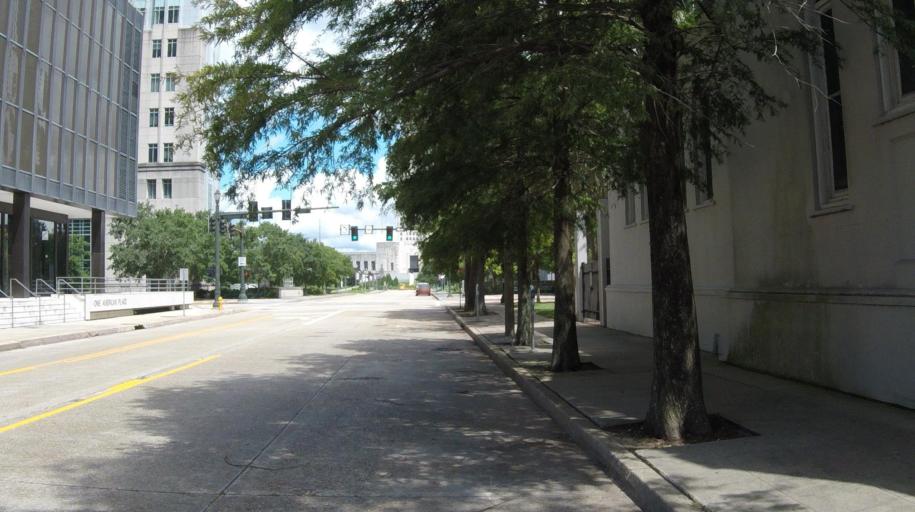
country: US
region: Louisiana
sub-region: West Baton Rouge Parish
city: Port Allen
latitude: 30.4519
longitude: -91.1872
